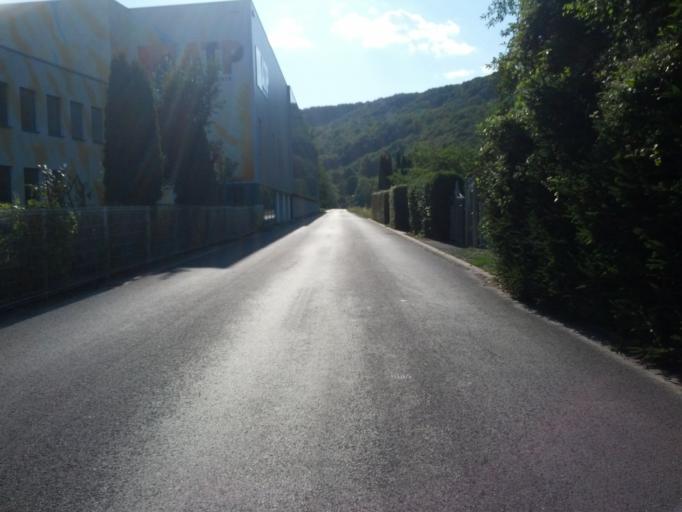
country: DE
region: Thuringia
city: Ebenshausen
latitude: 51.0735
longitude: 10.2776
